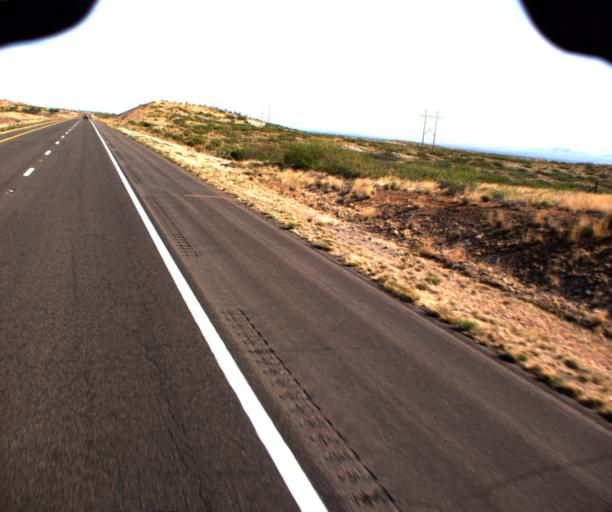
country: US
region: Arizona
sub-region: Graham County
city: Swift Trail Junction
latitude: 32.5060
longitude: -109.6739
